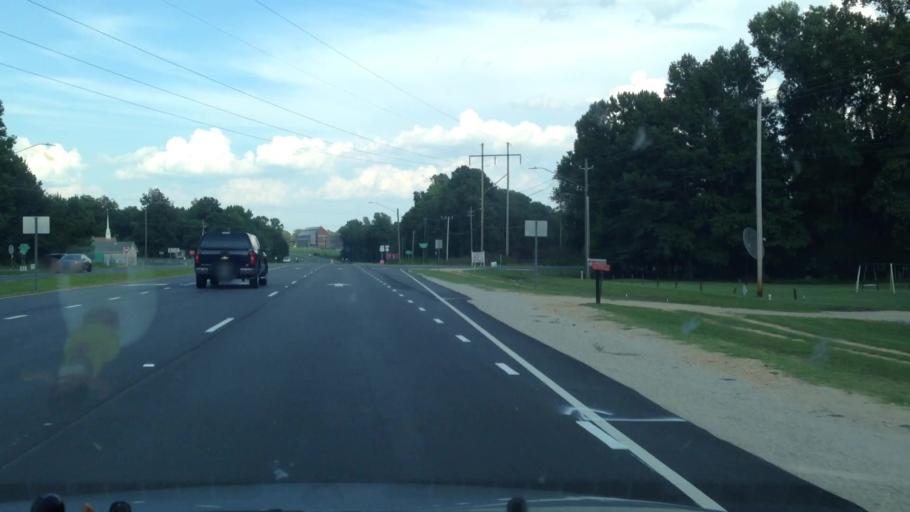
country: US
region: North Carolina
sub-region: Harnett County
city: Buies Creek
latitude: 35.4081
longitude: -78.7691
